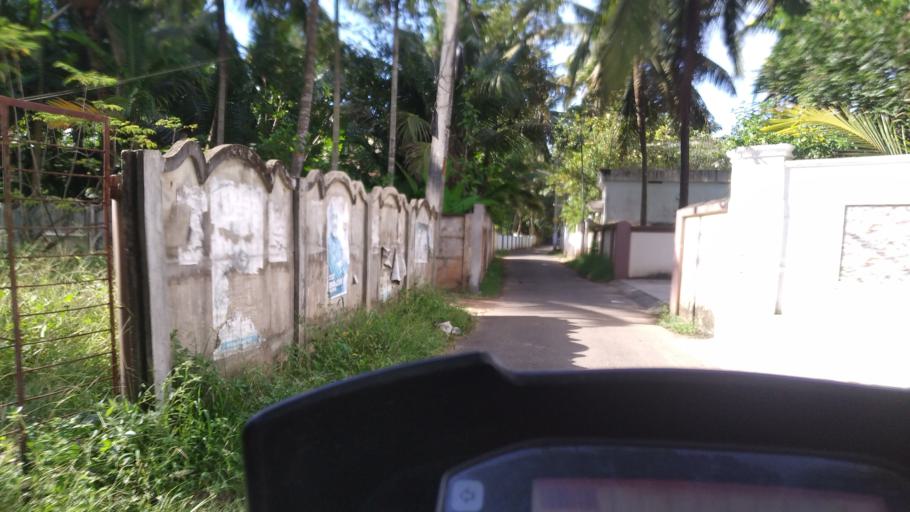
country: IN
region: Kerala
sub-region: Ernakulam
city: Elur
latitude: 10.0698
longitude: 76.2140
